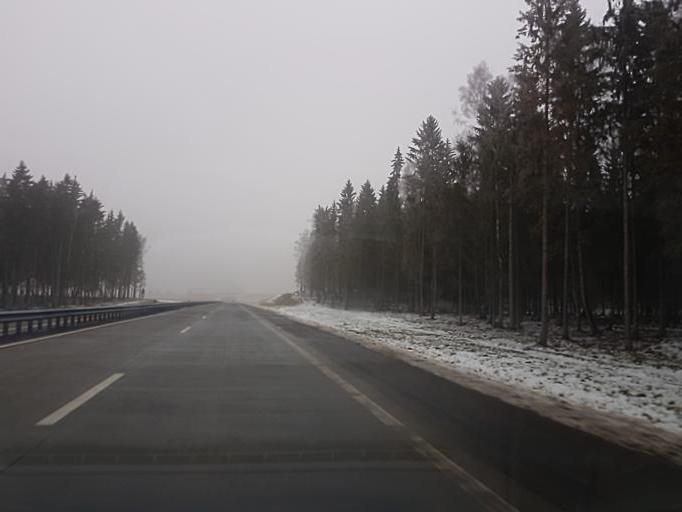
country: BY
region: Minsk
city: Atolina
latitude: 53.7240
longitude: 27.4283
